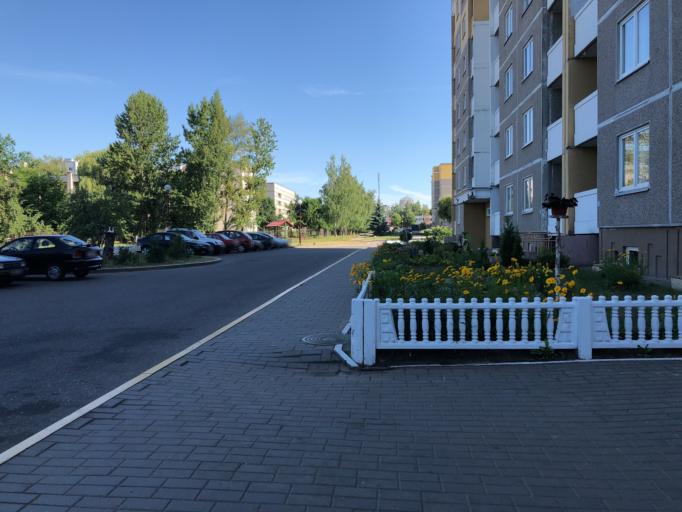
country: BY
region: Grodnenskaya
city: Hrodna
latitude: 53.6983
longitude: 23.8448
